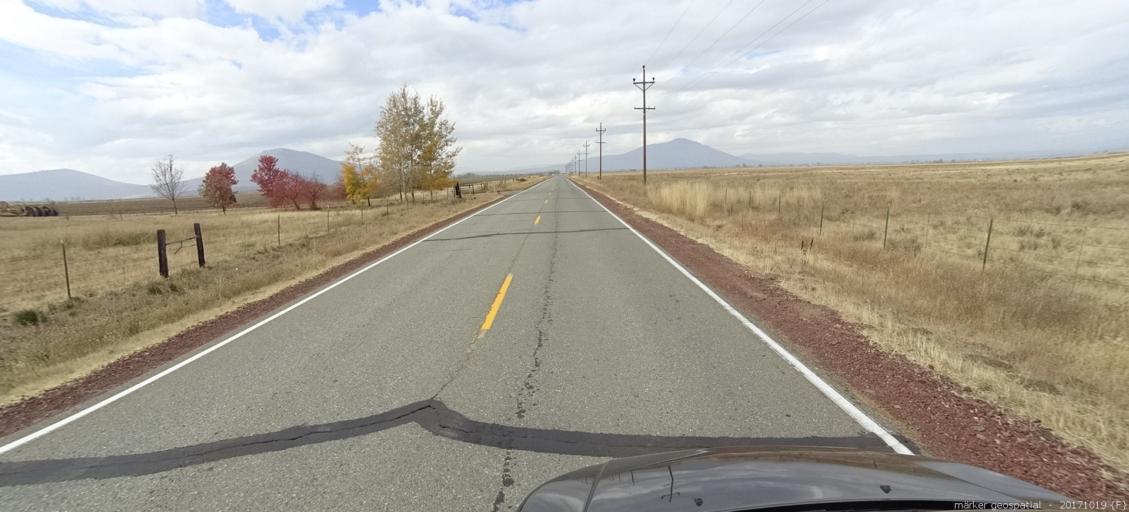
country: US
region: California
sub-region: Shasta County
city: Burney
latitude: 41.0509
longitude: -121.4168
